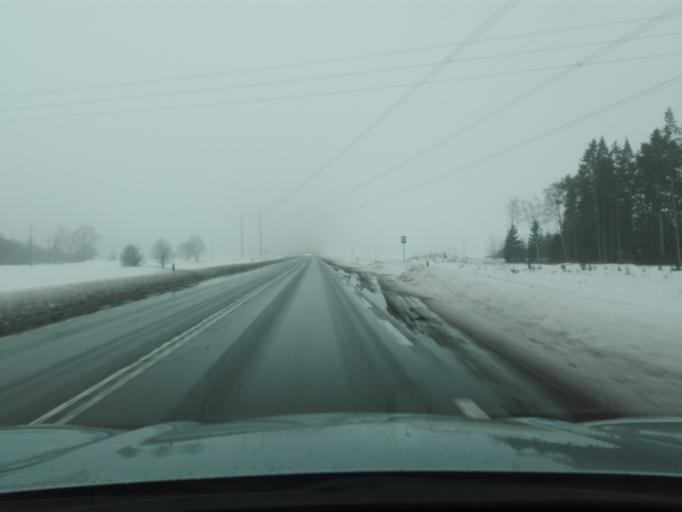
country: EE
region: Raplamaa
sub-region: Kohila vald
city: Kohila
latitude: 59.2139
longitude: 24.7770
